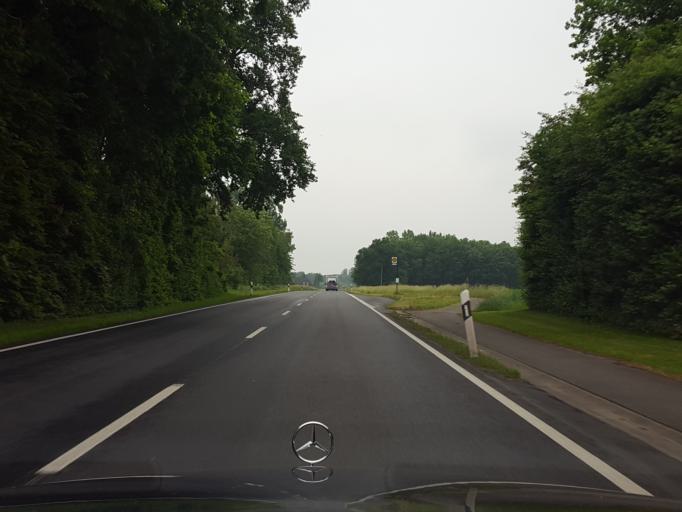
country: DE
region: North Rhine-Westphalia
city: Ludinghausen
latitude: 51.7381
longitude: 7.4176
